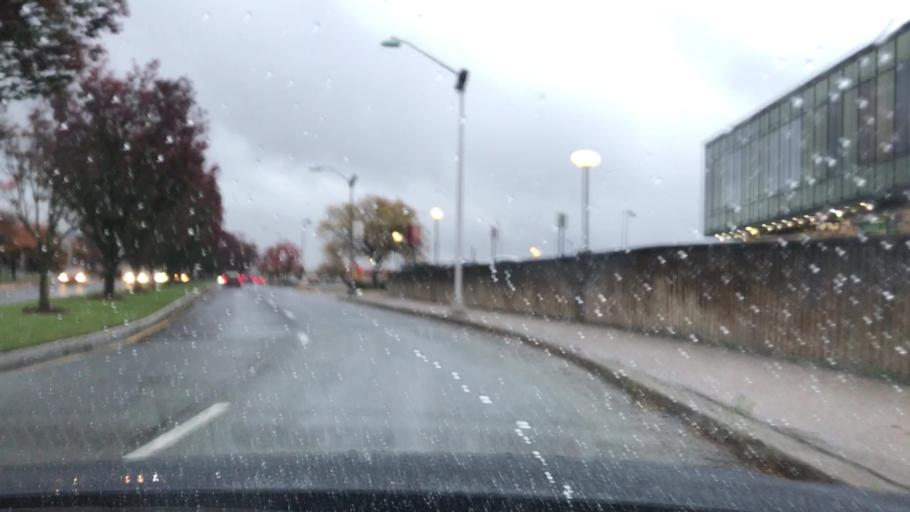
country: US
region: New Jersey
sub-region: Bergen County
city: Lodi
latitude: 40.8738
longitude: -74.0880
